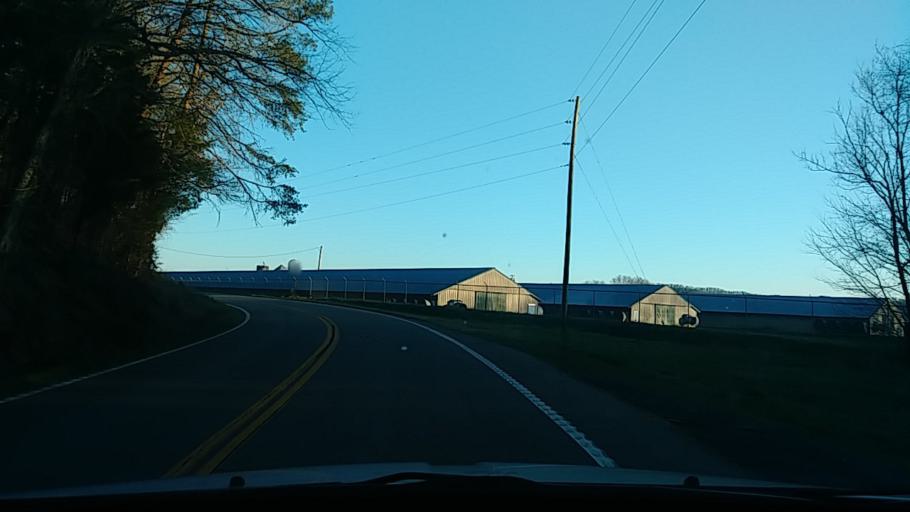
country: US
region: Tennessee
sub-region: Greene County
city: Mosheim
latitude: 36.1235
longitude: -83.0929
